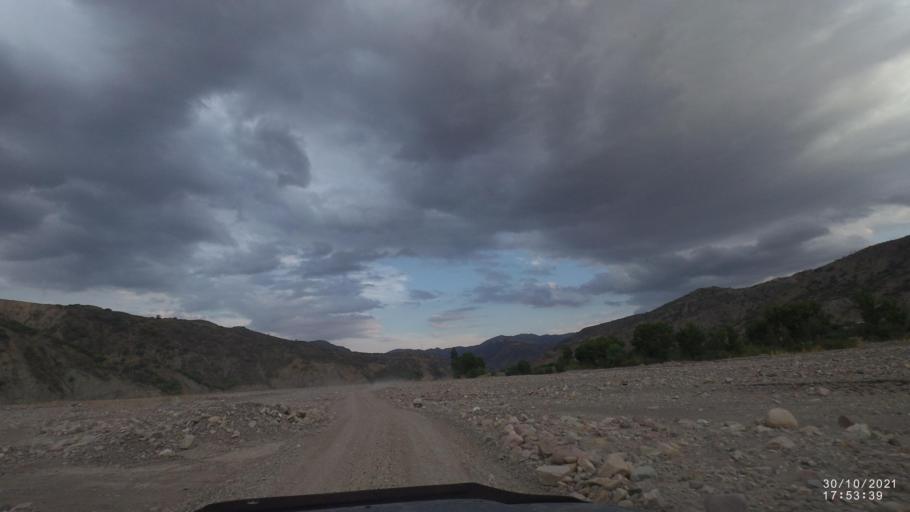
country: BO
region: Cochabamba
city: Sipe Sipe
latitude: -17.5397
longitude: -66.4940
